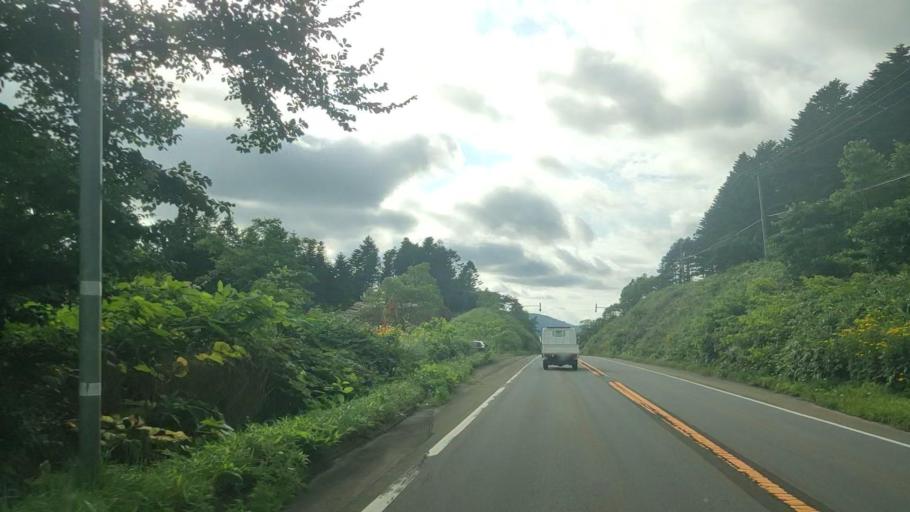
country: JP
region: Hokkaido
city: Niseko Town
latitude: 42.5973
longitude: 140.5025
